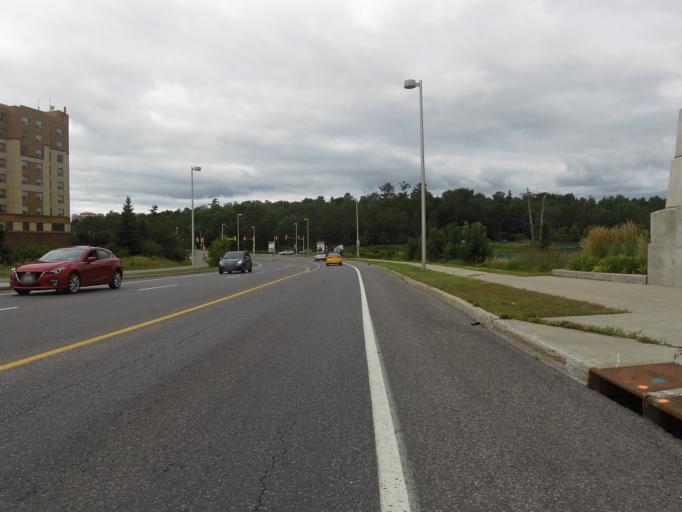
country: CA
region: Ontario
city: Bells Corners
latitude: 45.3118
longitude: -75.9036
